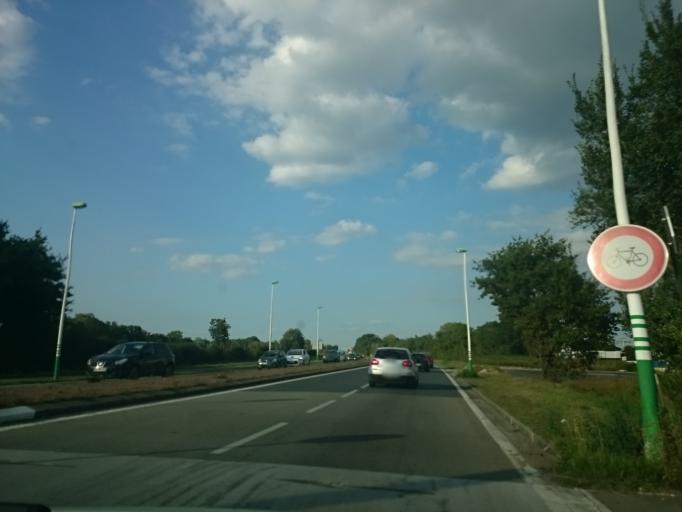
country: FR
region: Pays de la Loire
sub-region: Departement de la Loire-Atlantique
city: Saint-Herblain
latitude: 47.2203
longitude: -1.6552
